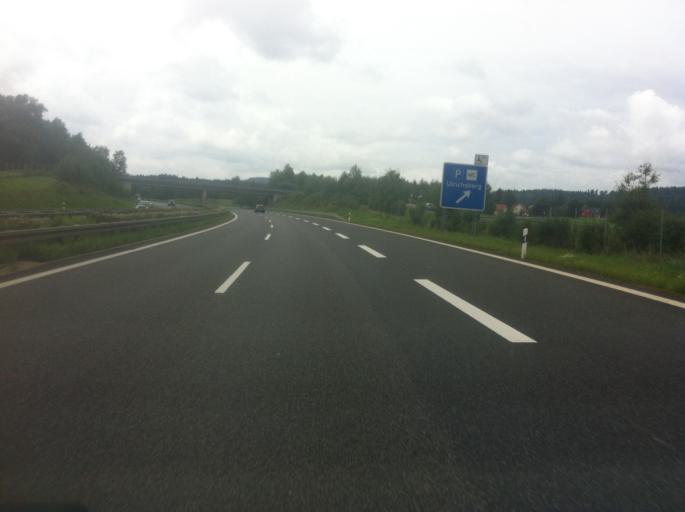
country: DE
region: Bavaria
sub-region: Upper Palatinate
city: Waidhaus
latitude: 49.6334
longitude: 12.4584
